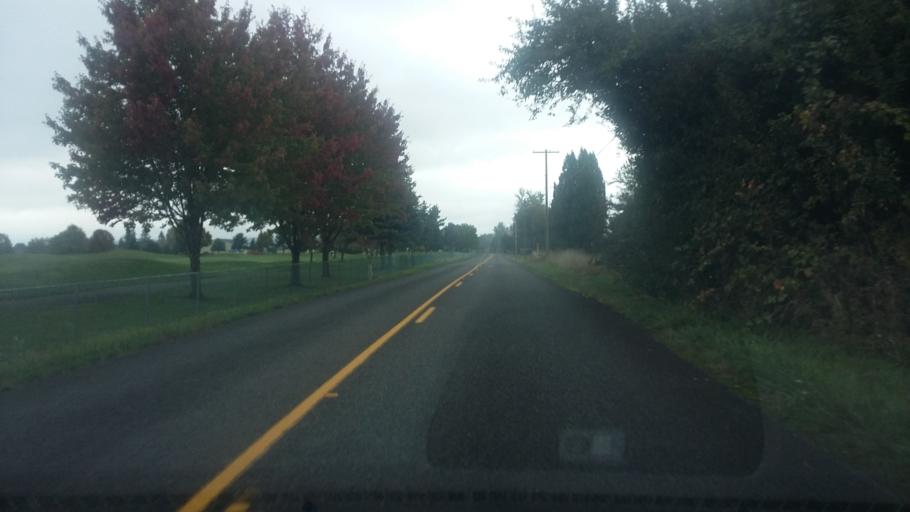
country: US
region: Washington
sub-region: Clark County
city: La Center
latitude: 45.8315
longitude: -122.6825
